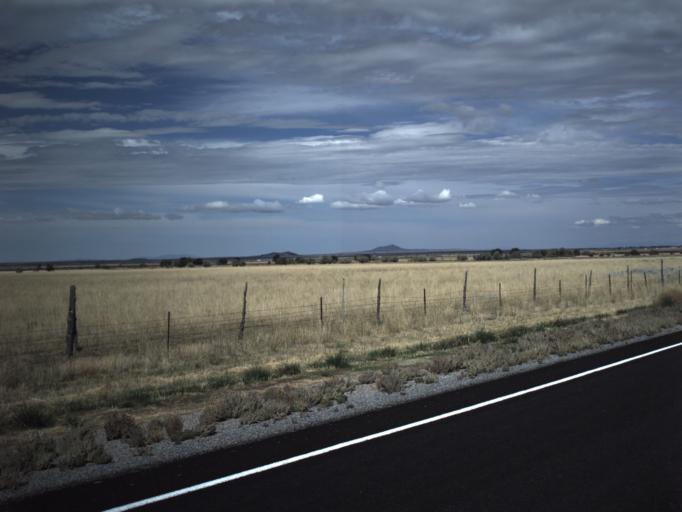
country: US
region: Utah
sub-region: Millard County
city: Fillmore
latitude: 38.8330
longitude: -112.4291
